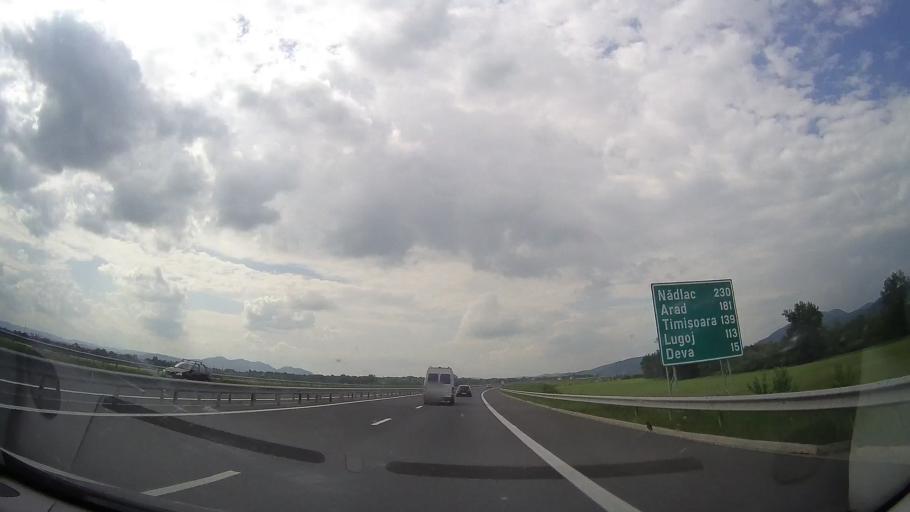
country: RO
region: Hunedoara
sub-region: Oras Simeria
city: Simeria
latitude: 45.8529
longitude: 23.0359
